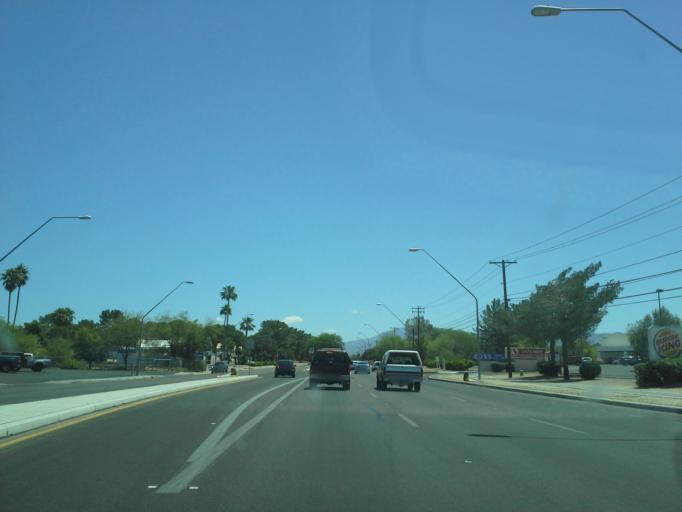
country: US
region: Arizona
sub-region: Pima County
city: Tucson
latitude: 32.2506
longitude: -110.8740
